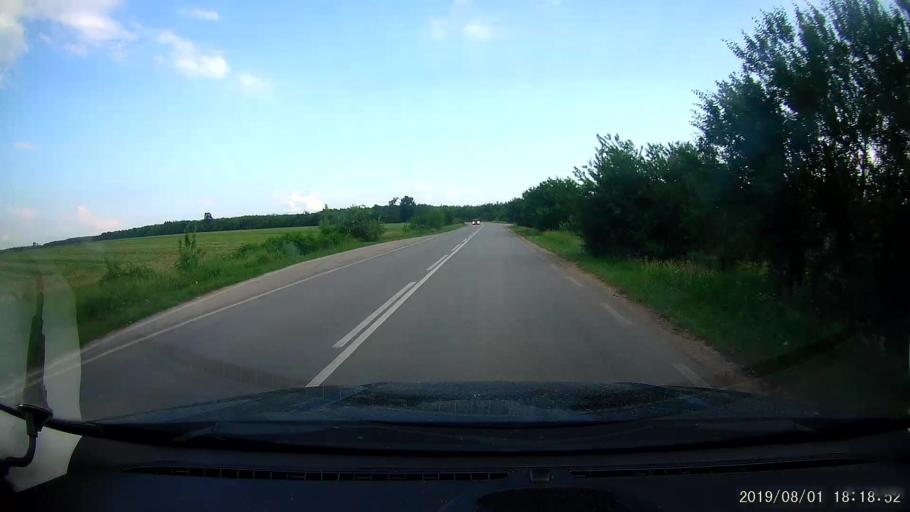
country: BG
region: Shumen
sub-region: Obshtina Kaolinovo
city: Kaolinovo
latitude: 43.6916
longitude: 27.0854
